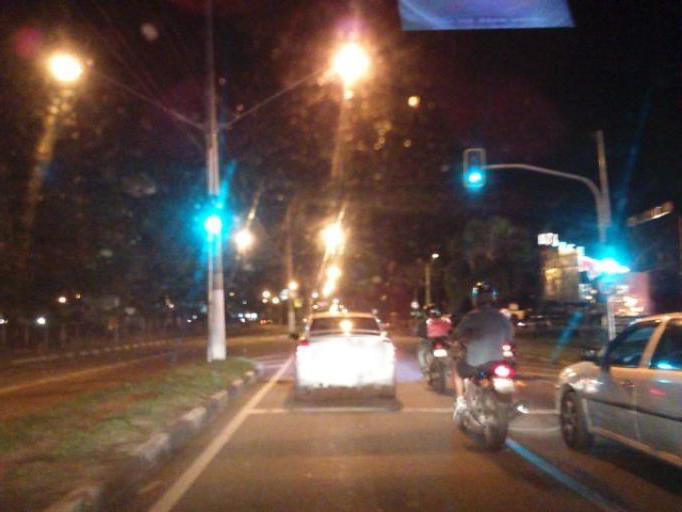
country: BR
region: Sao Paulo
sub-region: Jacarei
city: Jacarei
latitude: -23.2868
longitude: -45.9533
